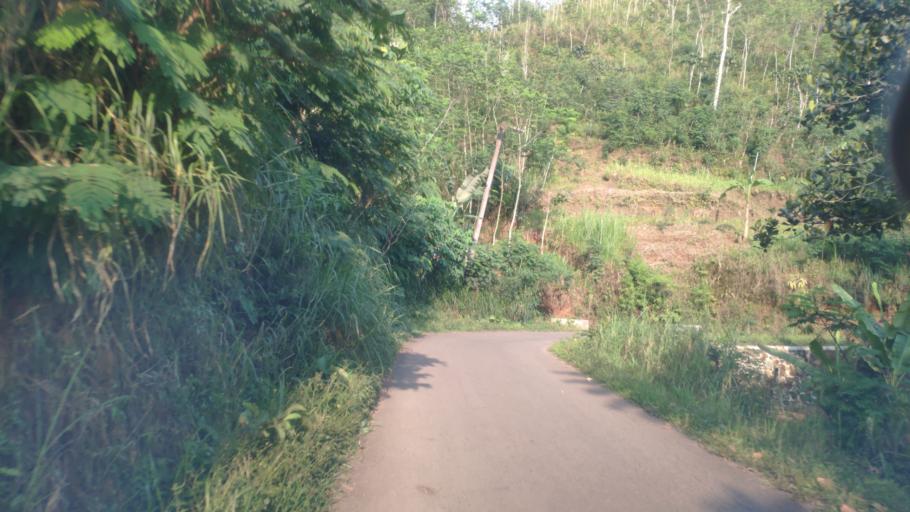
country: ID
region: Central Java
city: Wonosobo
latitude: -7.2545
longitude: 109.6890
